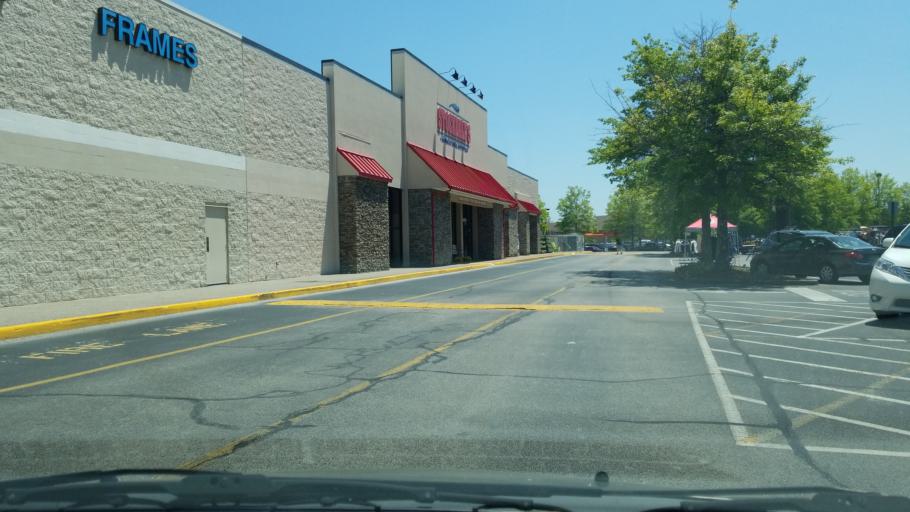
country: US
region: Tennessee
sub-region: Hamilton County
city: Red Bank
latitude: 35.1397
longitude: -85.2446
